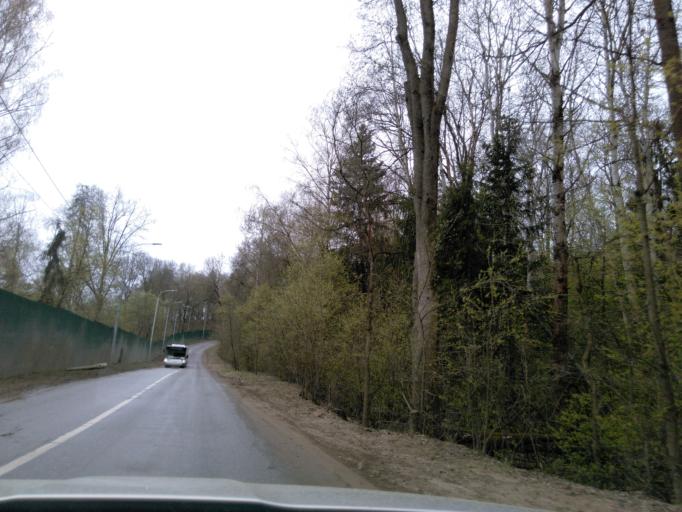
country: RU
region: Moskovskaya
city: Novopodrezkovo
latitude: 55.9075
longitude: 37.3575
